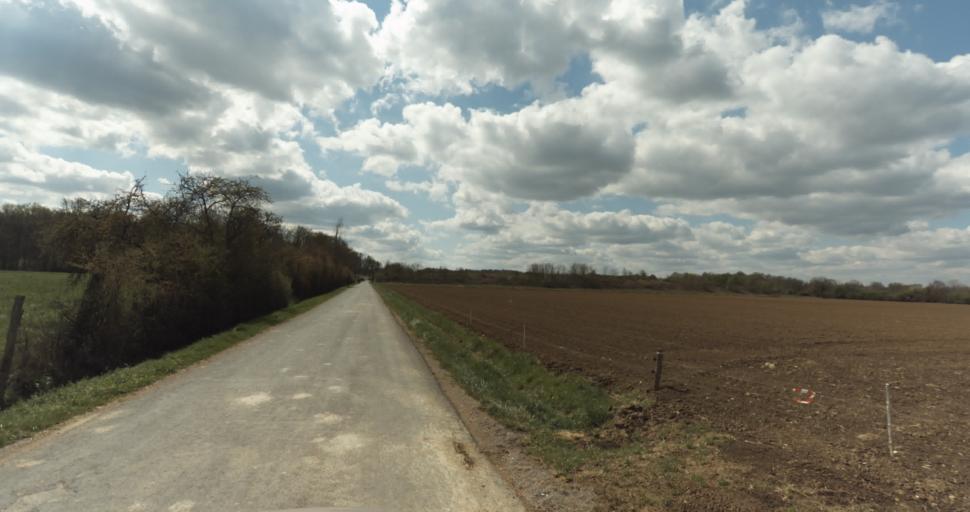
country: FR
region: Bourgogne
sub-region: Departement de la Cote-d'Or
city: Auxonne
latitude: 47.1953
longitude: 5.4230
